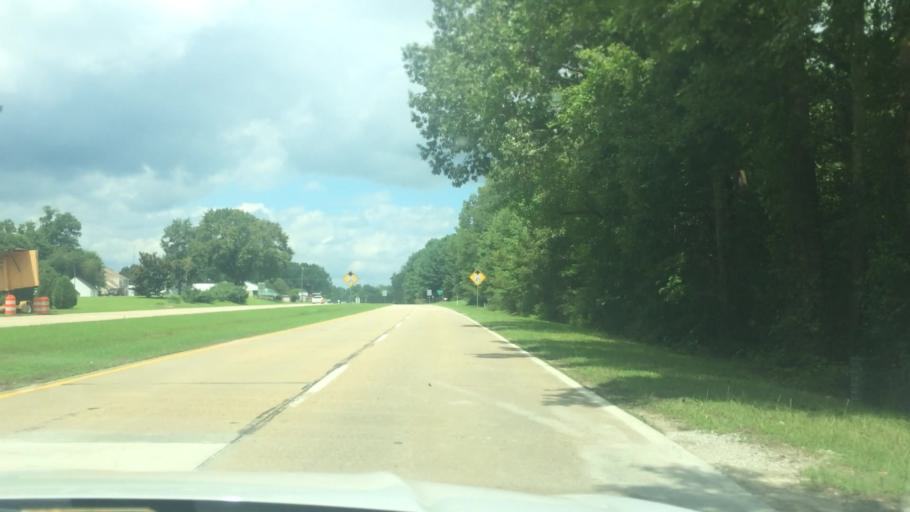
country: US
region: Virginia
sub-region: New Kent County
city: New Kent
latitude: 37.4409
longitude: -77.0323
